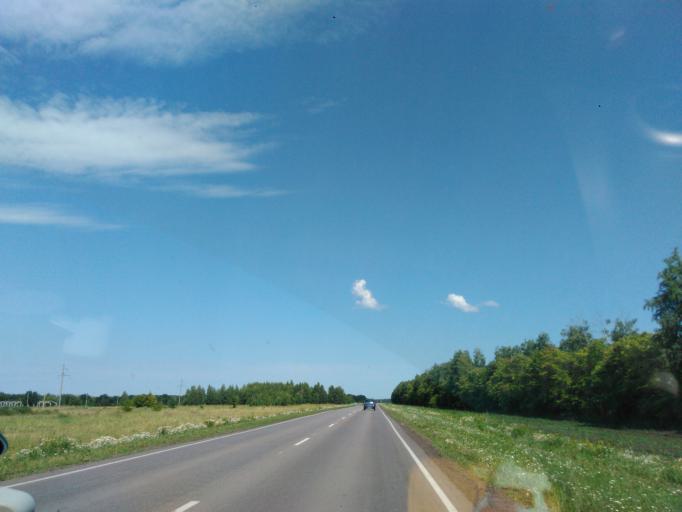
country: RU
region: Penza
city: Belinskiy
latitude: 52.9683
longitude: 43.4678
